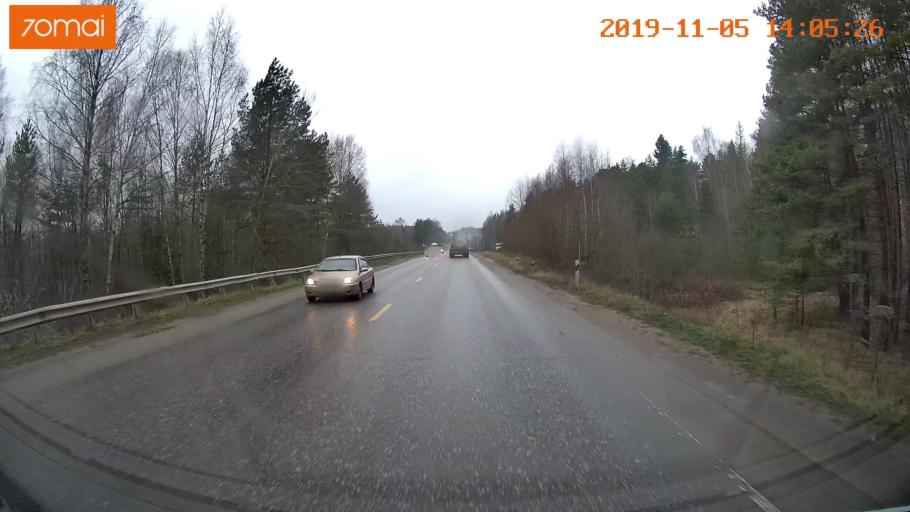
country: RU
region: Ivanovo
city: Kokhma
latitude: 56.9977
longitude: 41.1579
